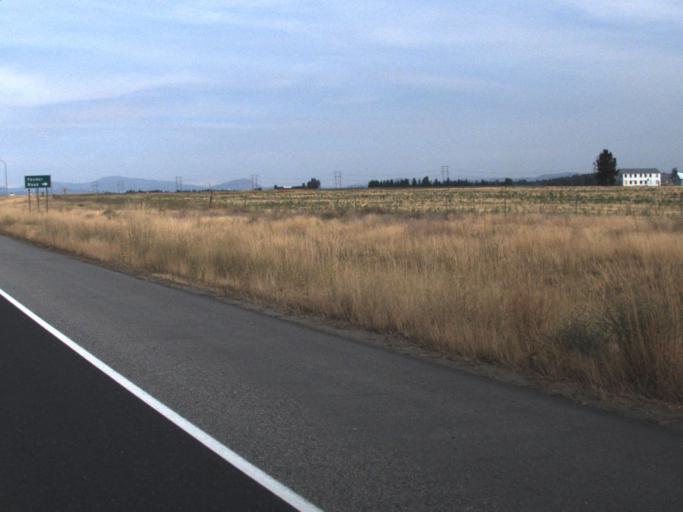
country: US
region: Washington
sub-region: Spokane County
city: Fairwood
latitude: 47.8358
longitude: -117.4213
